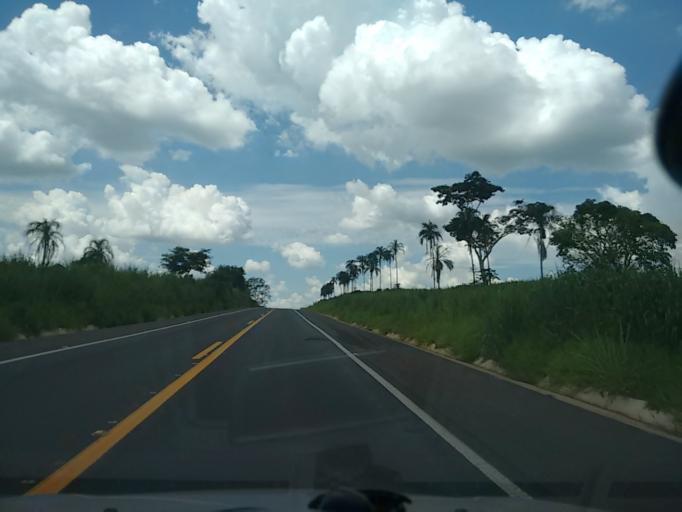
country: BR
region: Sao Paulo
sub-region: Osvaldo Cruz
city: Osvaldo Cruz
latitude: -21.8459
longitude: -50.8326
